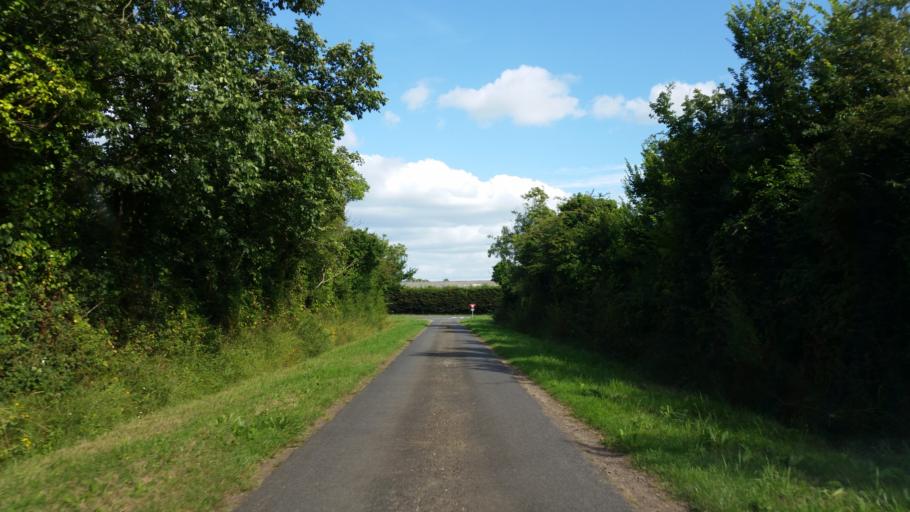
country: FR
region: Lower Normandy
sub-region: Departement de la Manche
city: Sainte-Mere-Eglise
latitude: 49.4506
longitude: -1.2772
